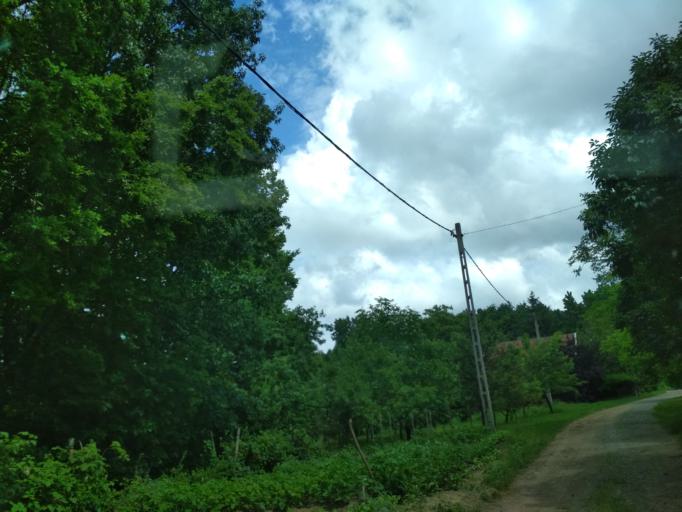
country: HU
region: Jasz-Nagykun-Szolnok
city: Tiszafured
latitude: 47.6183
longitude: 20.7310
